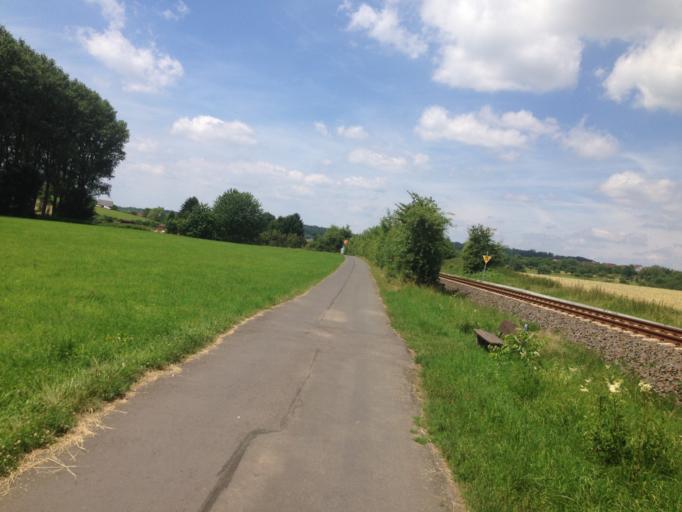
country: DE
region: Hesse
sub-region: Regierungsbezirk Giessen
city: Reiskirchen
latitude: 50.5980
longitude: 8.8428
